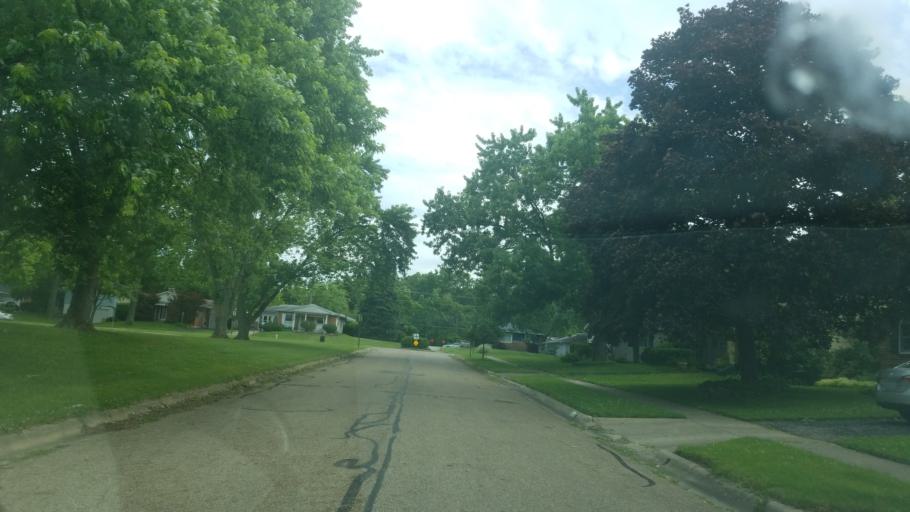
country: US
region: Ohio
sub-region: Franklin County
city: Worthington
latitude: 40.0734
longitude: -83.0078
